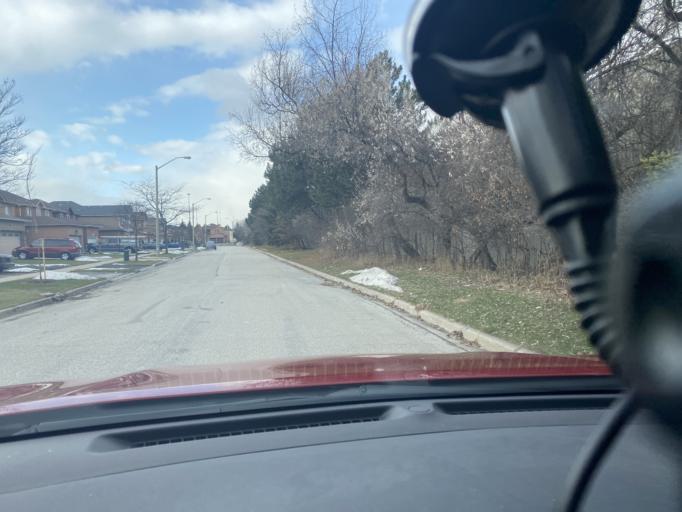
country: CA
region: Ontario
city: Scarborough
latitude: 43.7975
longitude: -79.1623
